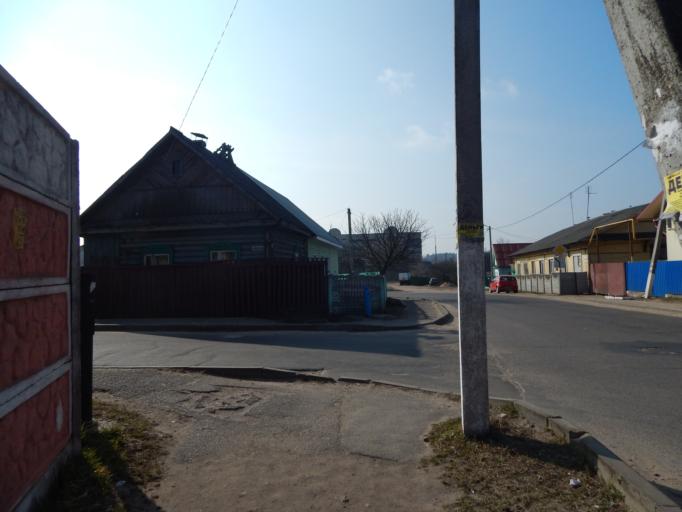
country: BY
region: Minsk
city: Horad Barysaw
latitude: 54.2429
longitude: 28.5026
